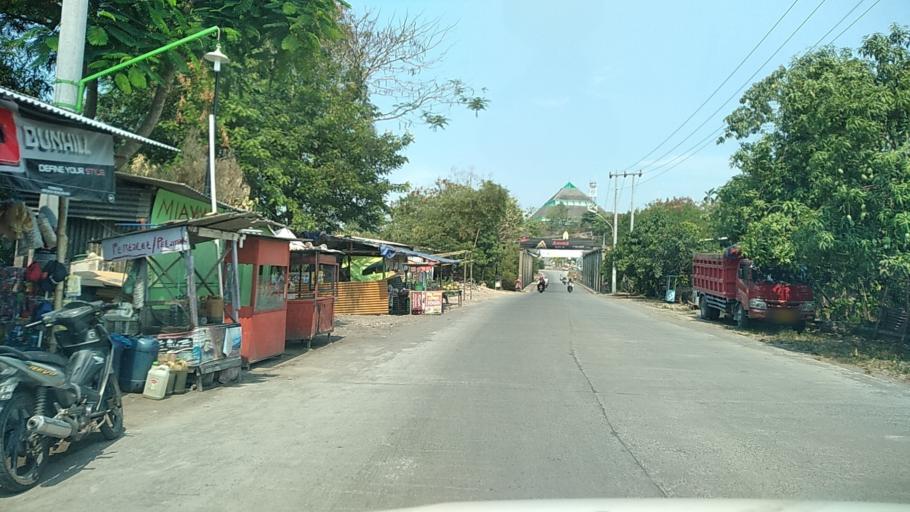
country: ID
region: Central Java
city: Mranggen
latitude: -7.0380
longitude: 110.4837
